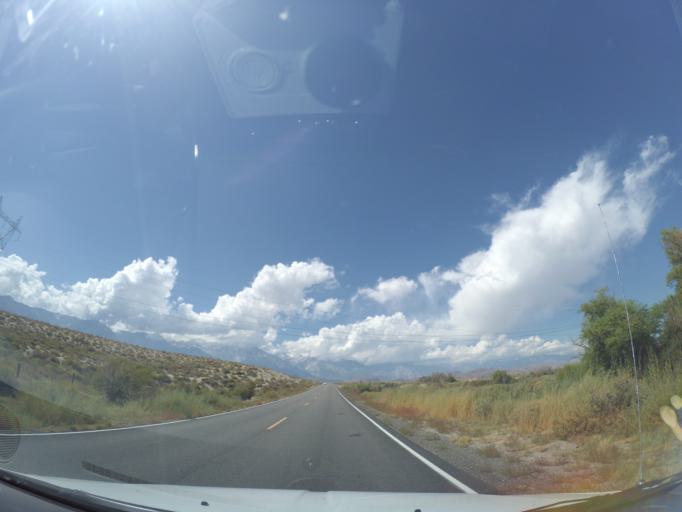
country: US
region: California
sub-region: Inyo County
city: Lone Pine
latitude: 36.5752
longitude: -118.0156
